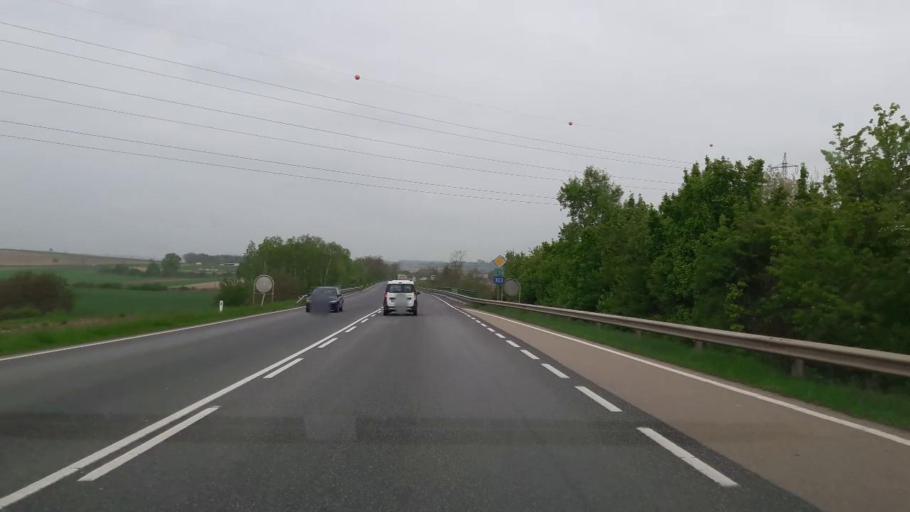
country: AT
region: Lower Austria
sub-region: Politischer Bezirk Hollabrunn
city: Hollabrunn
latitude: 48.5494
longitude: 16.0738
